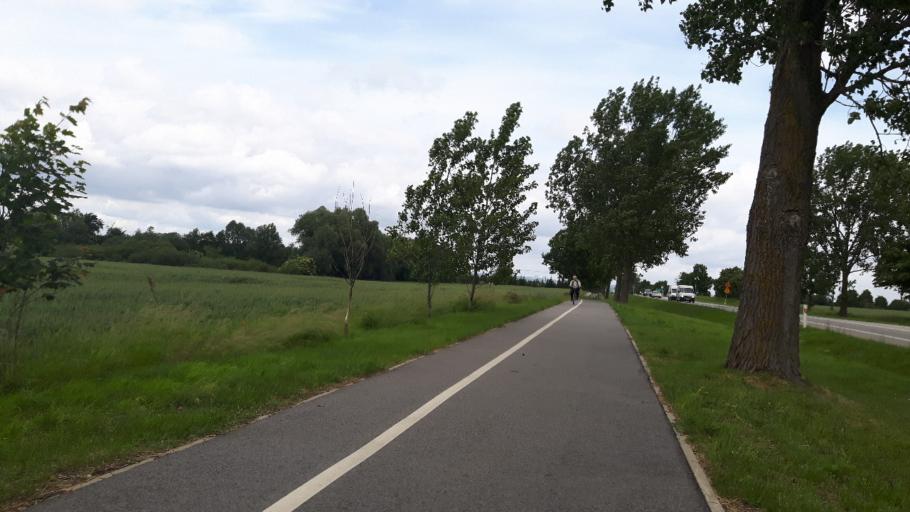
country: PL
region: West Pomeranian Voivodeship
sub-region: Powiat policki
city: Kolbaskowo
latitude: 53.3510
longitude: 14.4591
